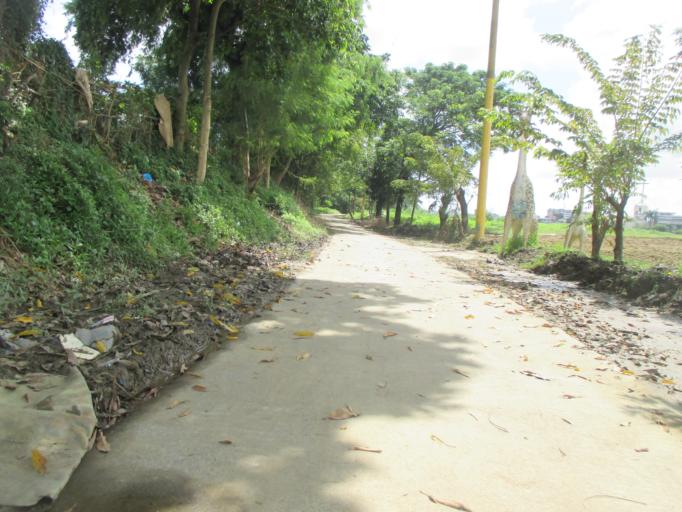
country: PH
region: Metro Manila
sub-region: Marikina
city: Calumpang
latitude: 14.6276
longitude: 121.0879
